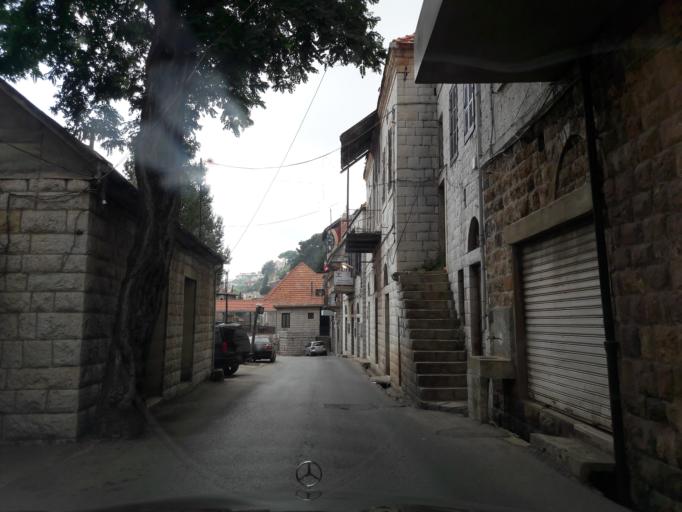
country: LB
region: Beqaa
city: Zahle
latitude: 33.9435
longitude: 35.7934
